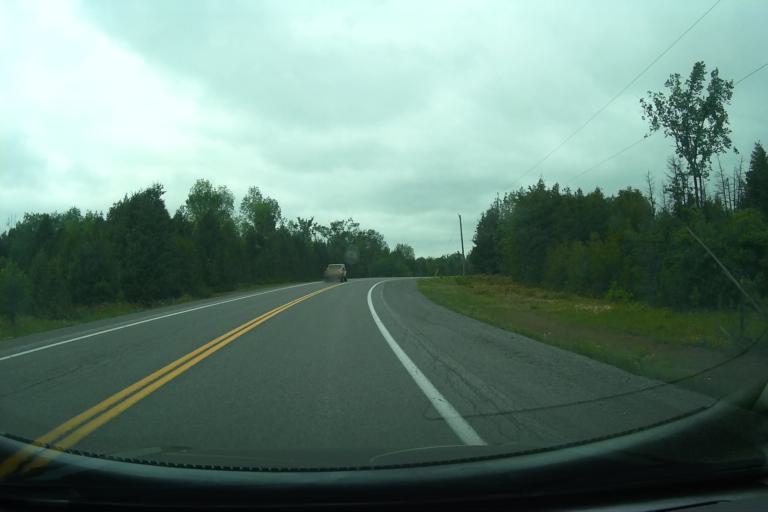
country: CA
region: Ontario
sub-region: Lanark County
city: Smiths Falls
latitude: 45.0219
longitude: -75.8556
